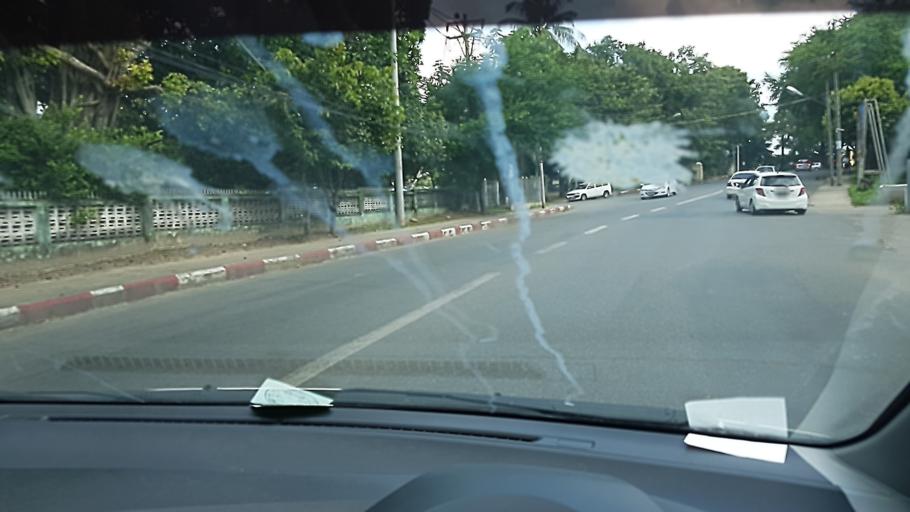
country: MM
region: Yangon
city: Yangon
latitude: 16.7913
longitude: 96.1670
